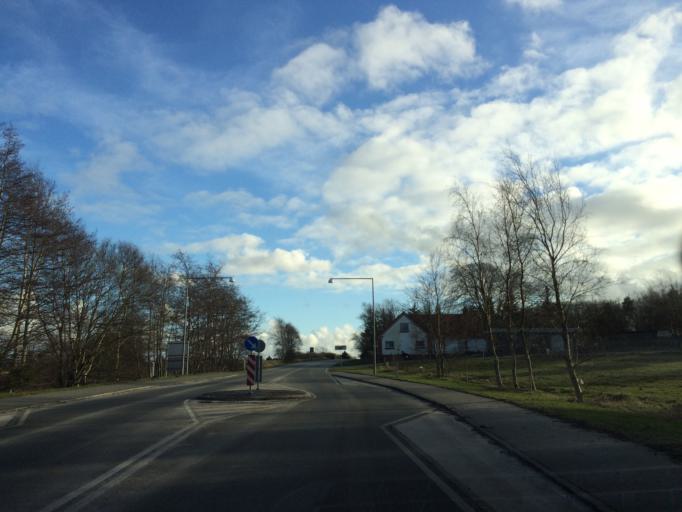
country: DK
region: Central Jutland
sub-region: Holstebro Kommune
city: Ulfborg
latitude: 56.4074
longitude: 8.3132
